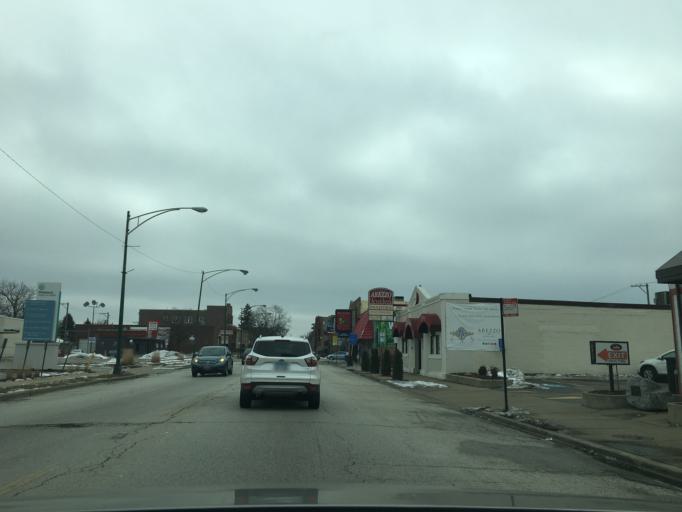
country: US
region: Illinois
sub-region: Cook County
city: Elmwood Park
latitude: 41.9373
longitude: -87.8067
